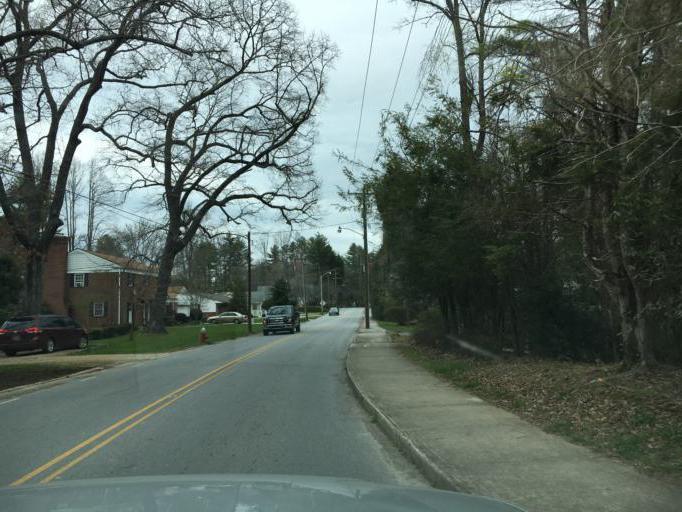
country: US
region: North Carolina
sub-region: Transylvania County
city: Brevard
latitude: 35.2307
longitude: -82.7246
